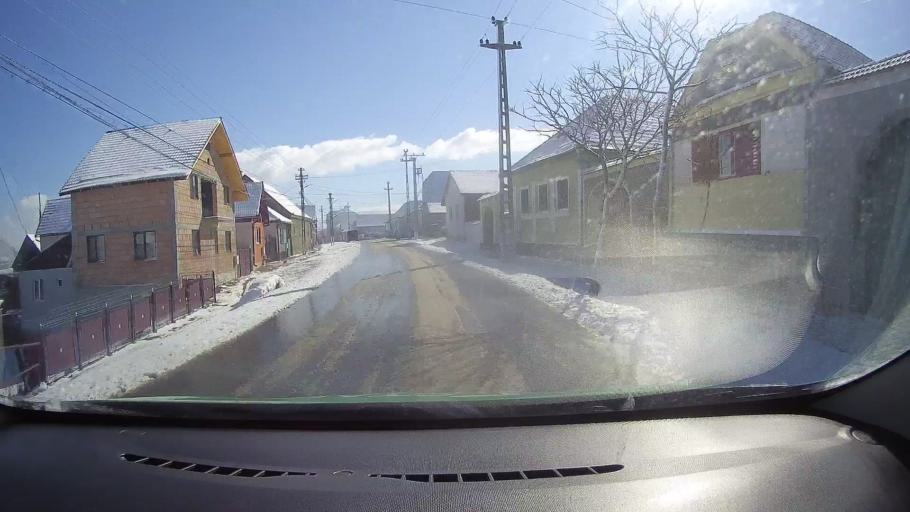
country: RO
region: Sibiu
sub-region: Comuna Rosia
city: Rosia
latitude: 45.8165
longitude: 24.3114
